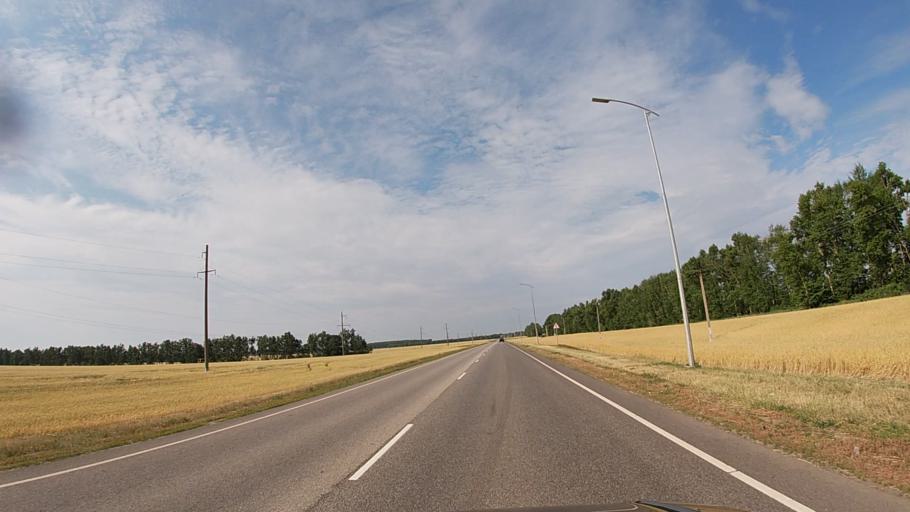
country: RU
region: Belgorod
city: Proletarskiy
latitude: 50.8153
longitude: 35.7516
